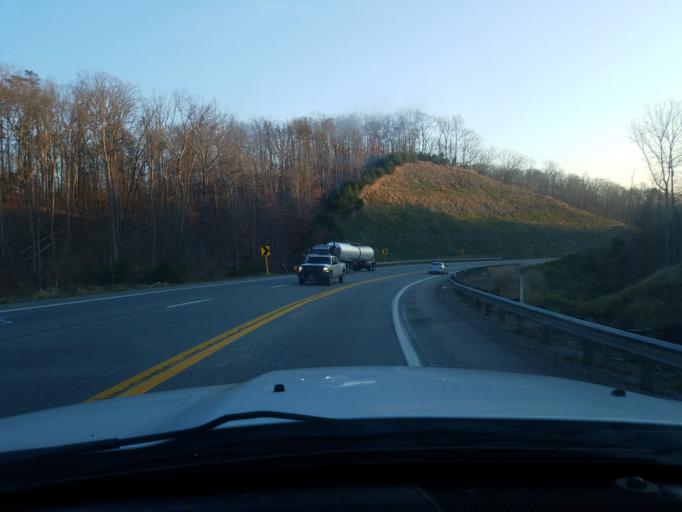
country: US
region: West Virginia
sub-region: Putnam County
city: Buffalo
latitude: 38.5789
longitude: -82.0157
